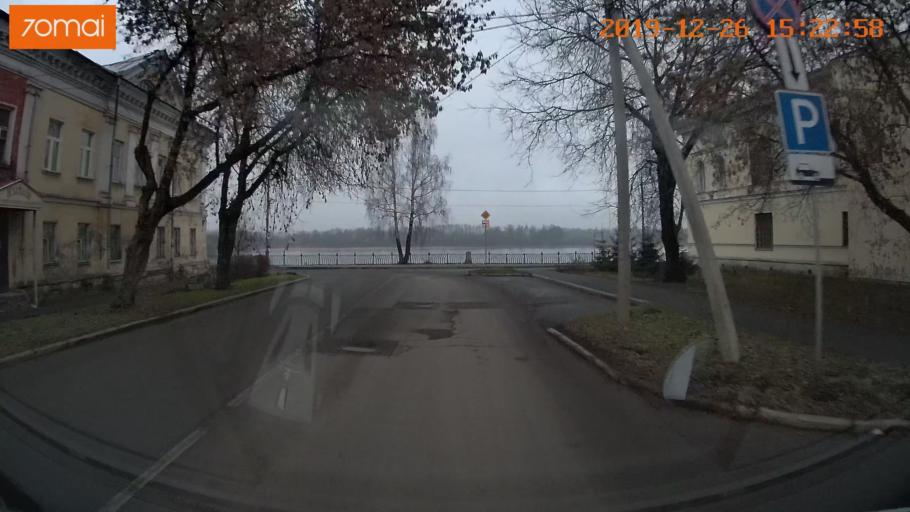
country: RU
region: Jaroslavl
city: Rybinsk
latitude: 58.0477
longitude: 38.8625
